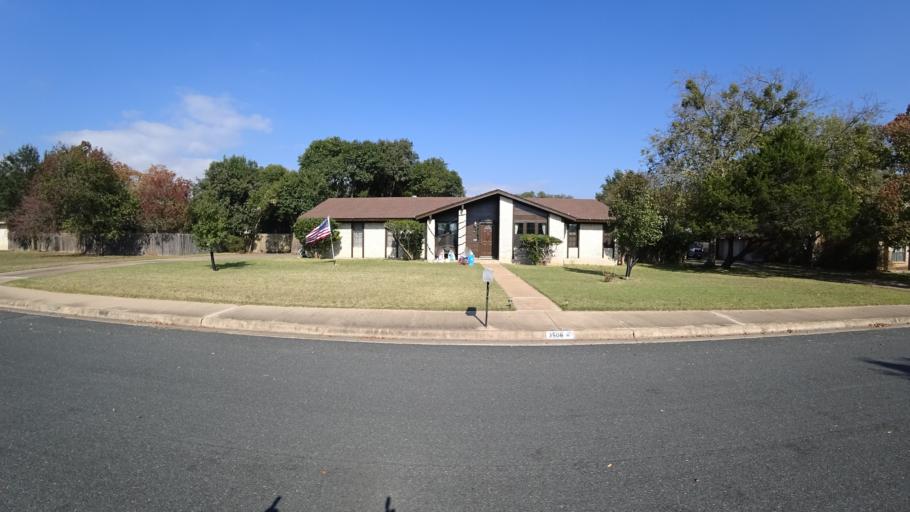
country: US
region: Texas
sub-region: Travis County
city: Shady Hollow
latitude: 30.1630
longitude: -97.8658
